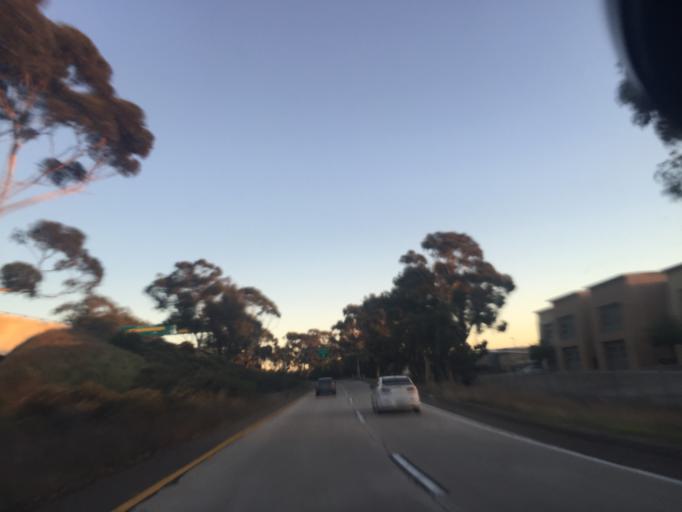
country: MX
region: Baja California
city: Tijuana
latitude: 32.5492
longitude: -117.0411
